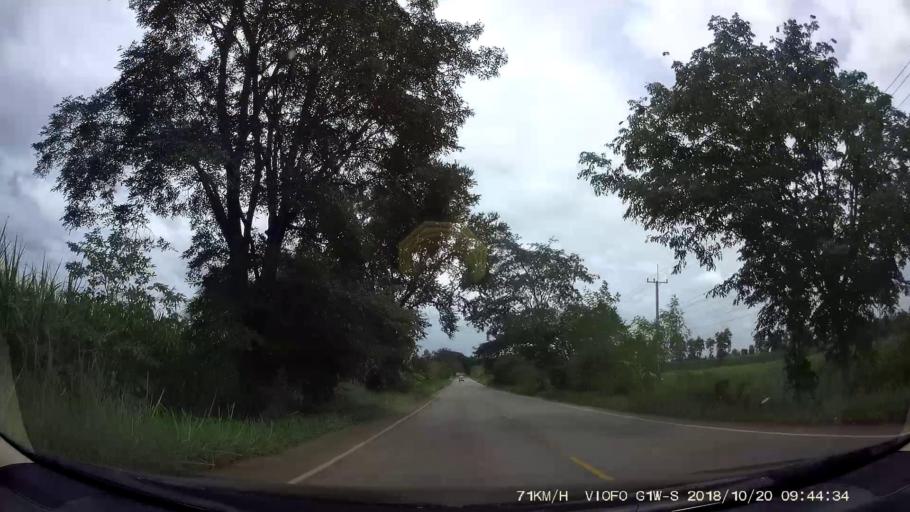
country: TH
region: Chaiyaphum
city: Khon San
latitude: 16.4844
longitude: 101.9433
